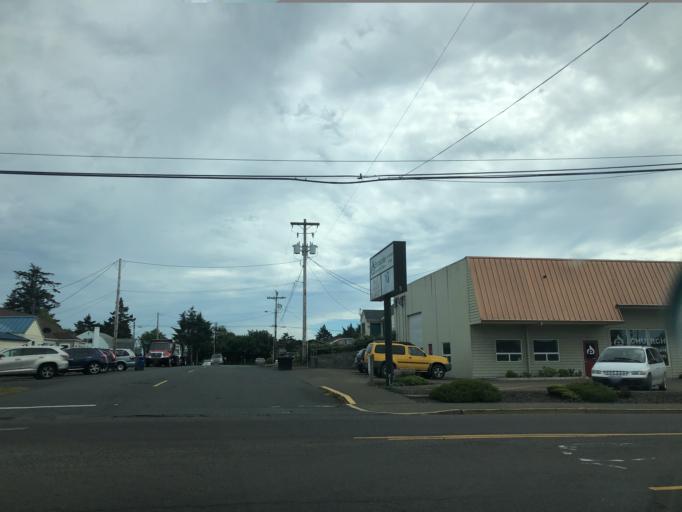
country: US
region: Oregon
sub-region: Lincoln County
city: Newport
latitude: 44.6364
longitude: -124.0494
